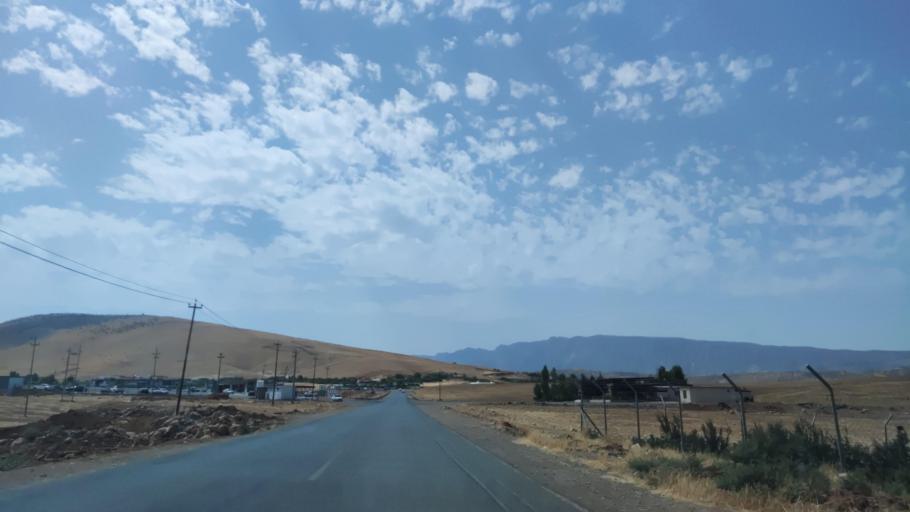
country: IQ
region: Arbil
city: Shaqlawah
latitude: 36.4722
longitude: 44.3974
